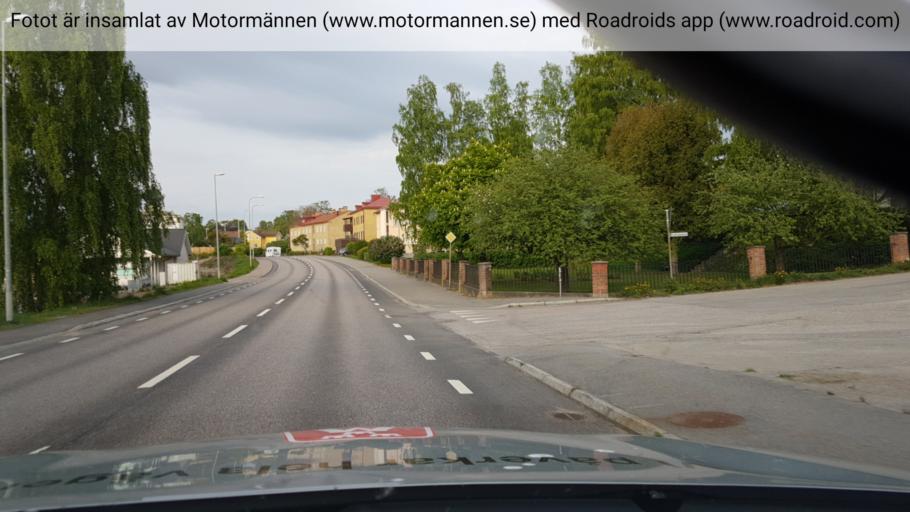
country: SE
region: Vaestmanland
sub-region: Kungsors Kommun
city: Kungsoer
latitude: 59.4241
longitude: 16.0844
